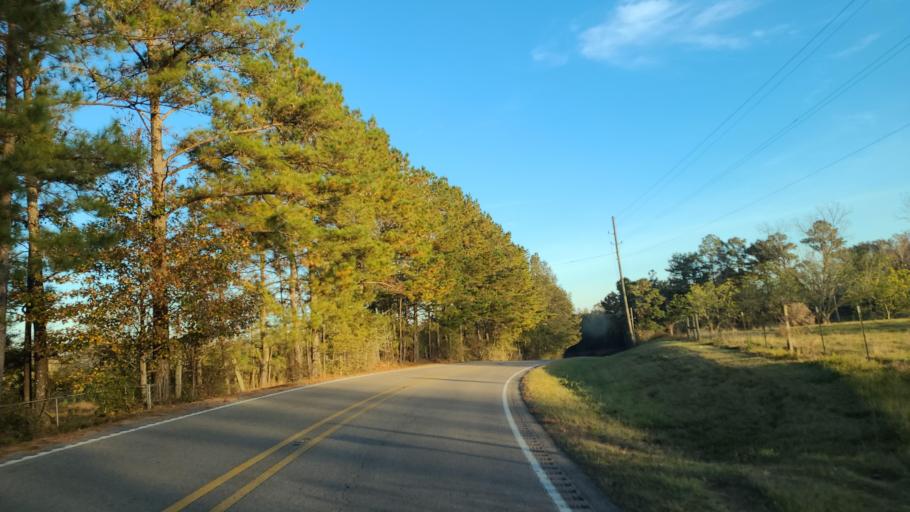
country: US
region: Mississippi
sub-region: Lamar County
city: Lumberton
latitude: 30.9955
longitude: -89.3851
